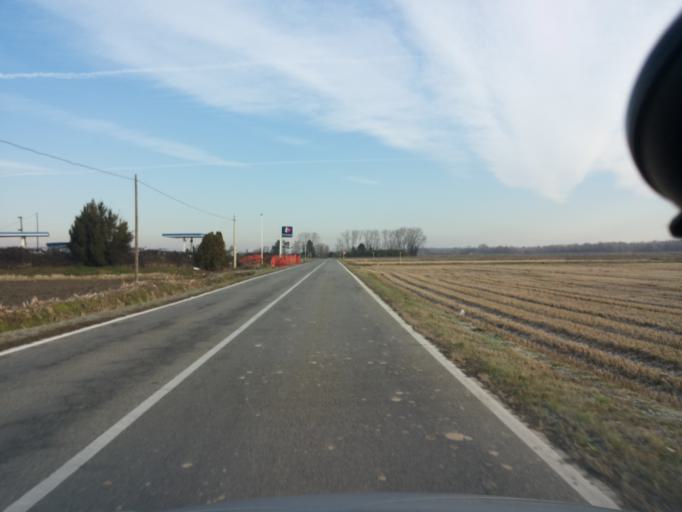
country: IT
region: Piedmont
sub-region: Provincia di Vercelli
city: Oldenico
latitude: 45.3903
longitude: 8.3771
